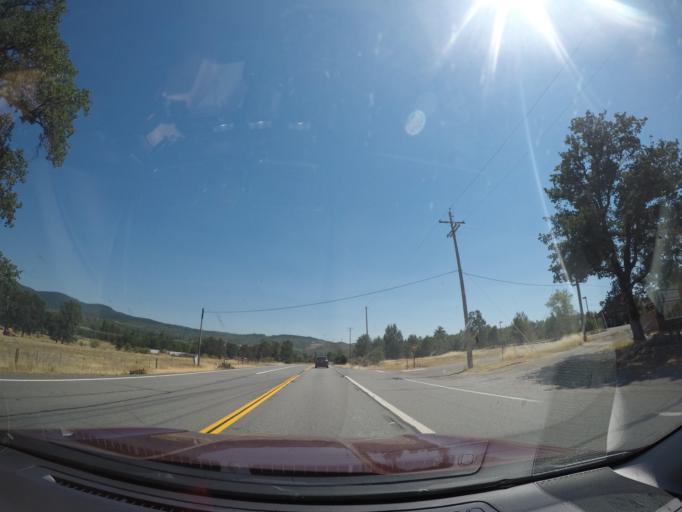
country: US
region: California
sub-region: Shasta County
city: Burney
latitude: 40.8038
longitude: -121.9398
